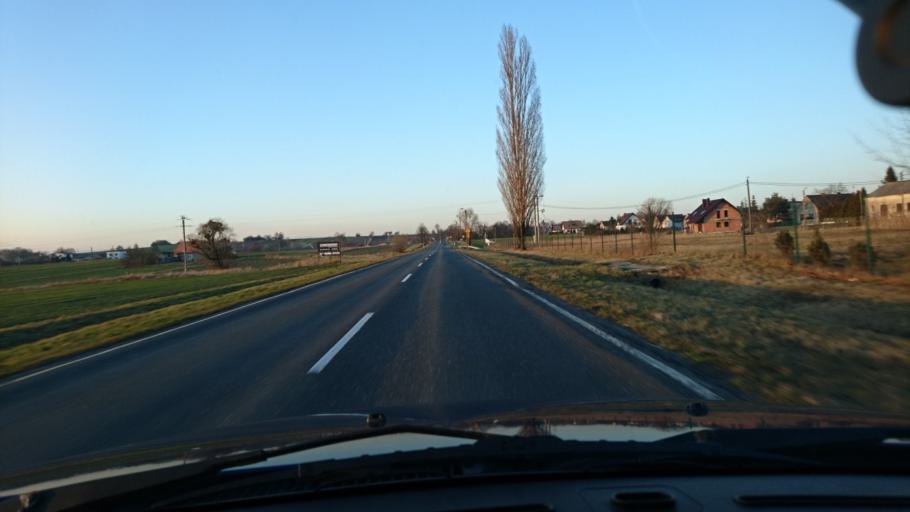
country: PL
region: Silesian Voivodeship
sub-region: Powiat gliwicki
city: Wielowies
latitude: 50.4700
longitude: 18.6103
